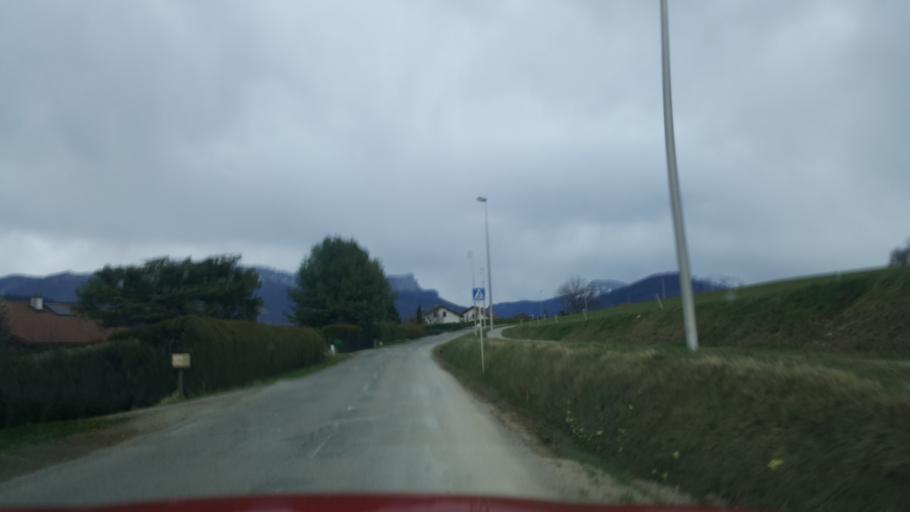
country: FR
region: Rhone-Alpes
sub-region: Departement de la Haute-Savoie
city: Epagny
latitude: 45.9476
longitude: 6.1002
